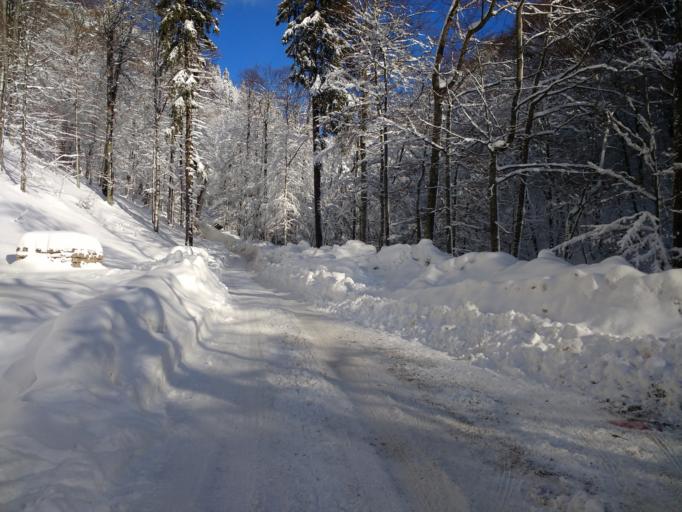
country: RO
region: Brasov
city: Crivina
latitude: 45.5013
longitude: 25.9423
